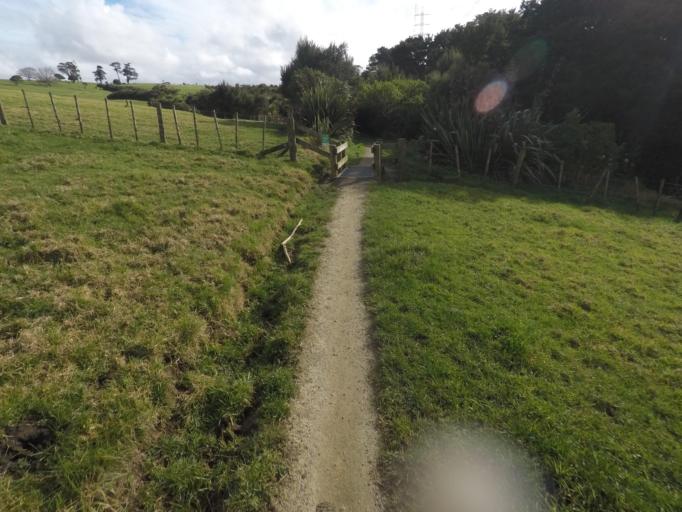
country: NZ
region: Auckland
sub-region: Auckland
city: Manukau City
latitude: -36.9937
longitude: 174.9098
